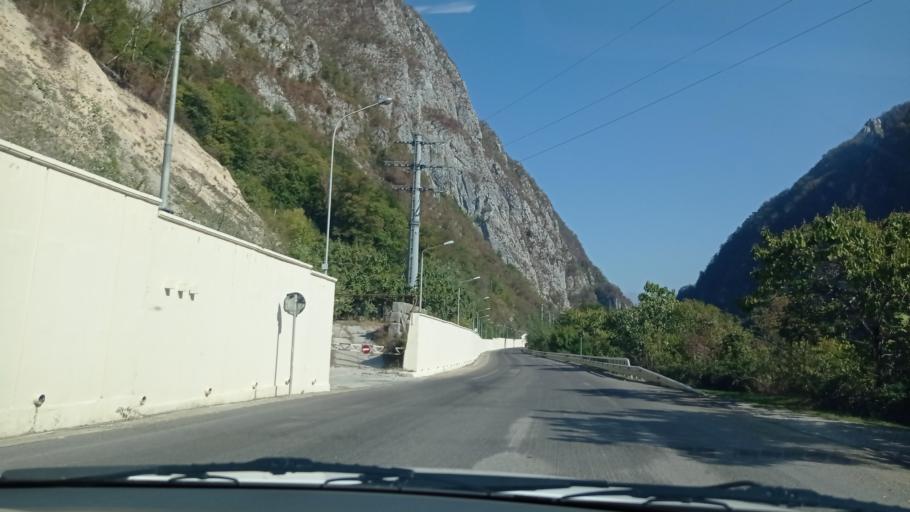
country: RU
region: Krasnodarskiy
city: Vysokoye
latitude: 43.5948
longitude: 40.0185
